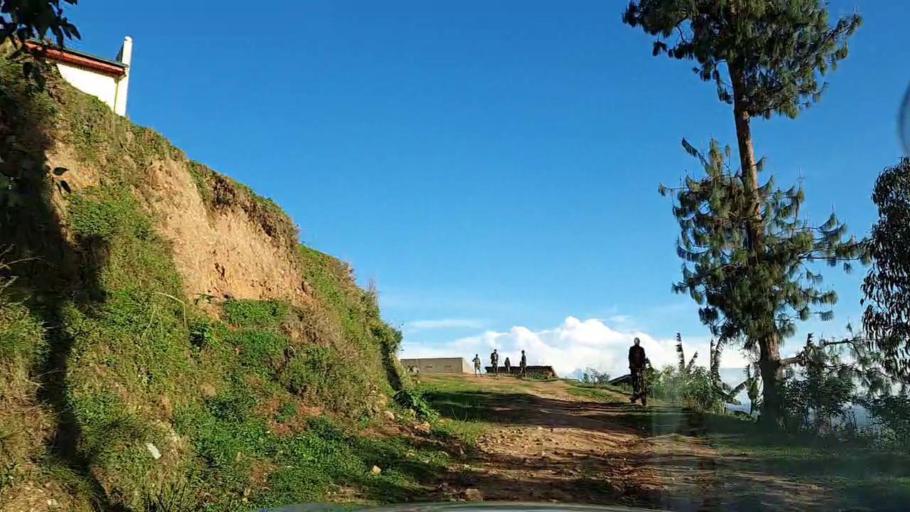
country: RW
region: Southern Province
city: Gikongoro
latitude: -2.4136
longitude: 29.5182
